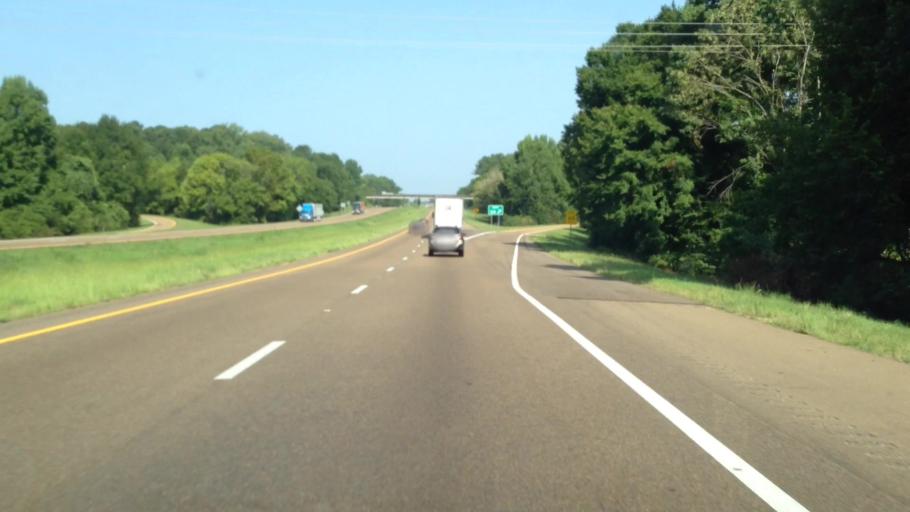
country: US
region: Mississippi
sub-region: Hinds County
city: Clinton
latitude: 32.3408
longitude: -90.3485
